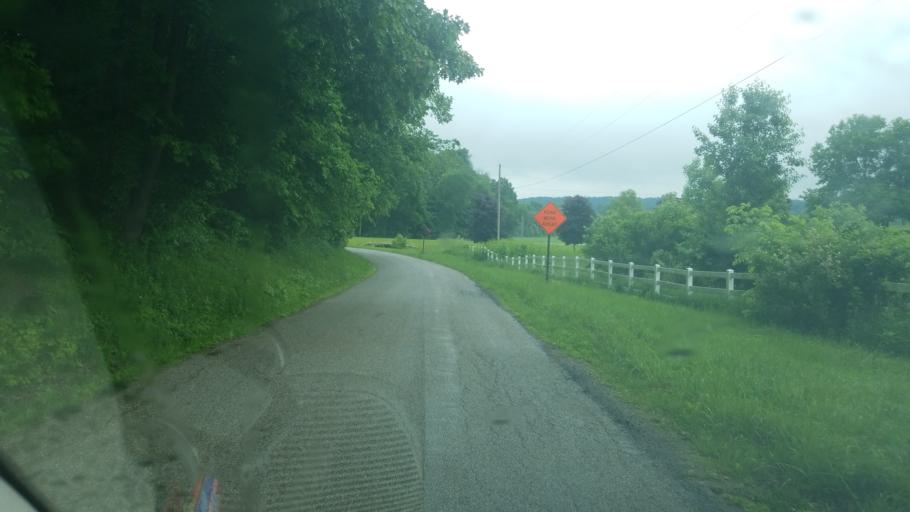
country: US
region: Ohio
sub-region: Sandusky County
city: Bellville
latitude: 40.6067
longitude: -82.4542
